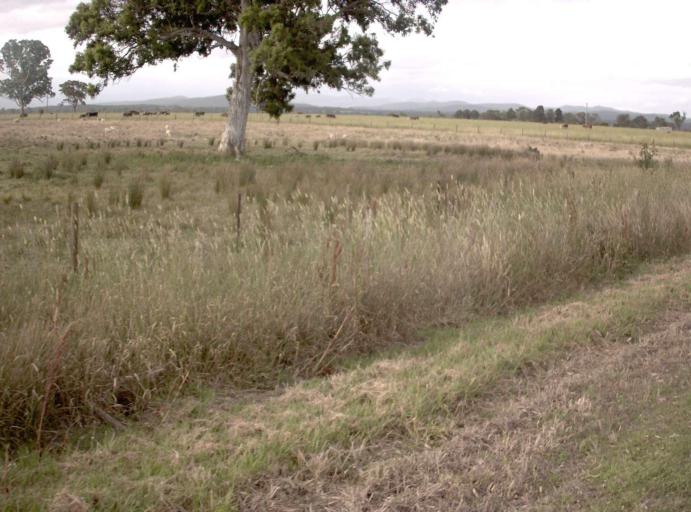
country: AU
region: Victoria
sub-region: Wellington
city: Sale
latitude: -37.8542
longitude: 147.0441
